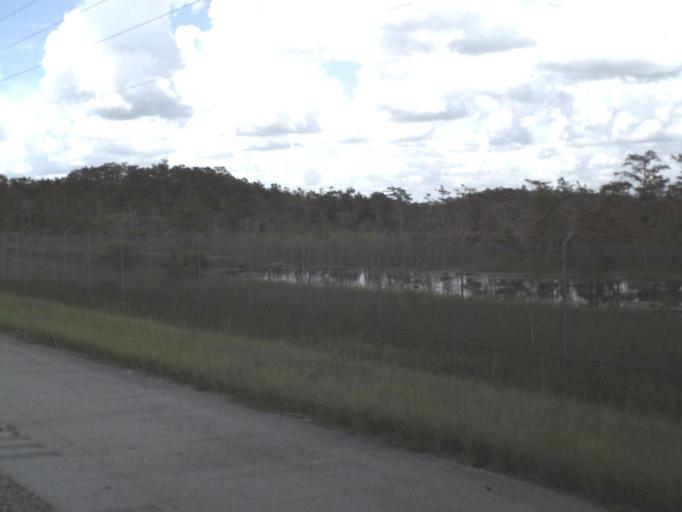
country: US
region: Florida
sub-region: Collier County
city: Immokalee
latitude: 26.1693
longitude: -81.0444
